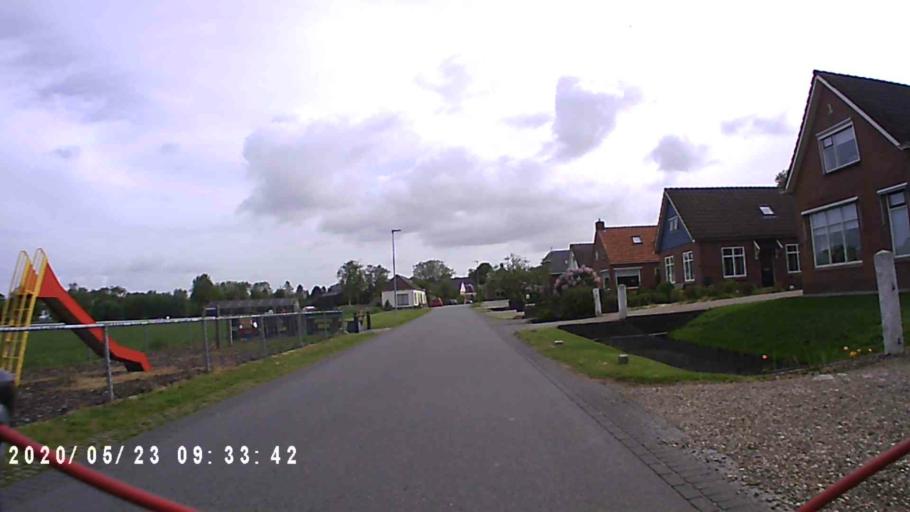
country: NL
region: Groningen
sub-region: Gemeente Slochteren
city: Slochteren
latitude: 53.3004
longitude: 6.7235
